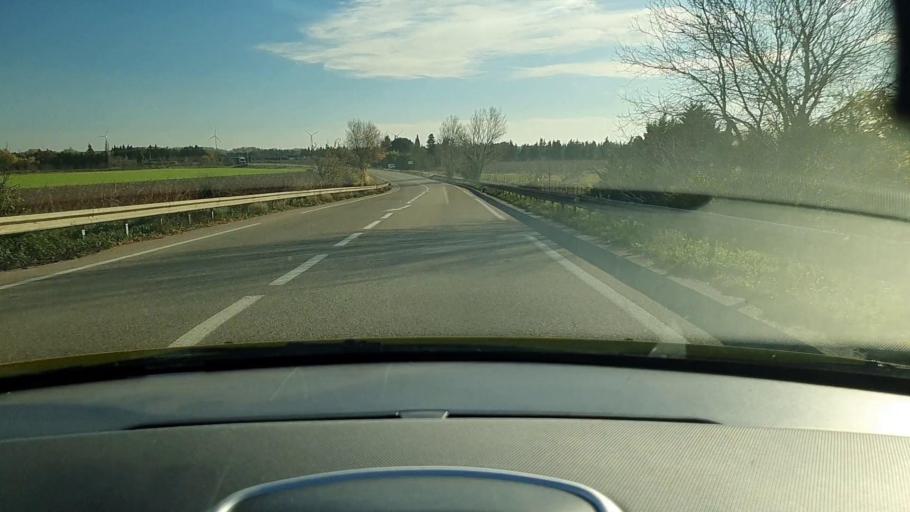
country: FR
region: Languedoc-Roussillon
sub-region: Departement du Gard
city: Beaucaire
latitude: 43.7958
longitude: 4.6103
